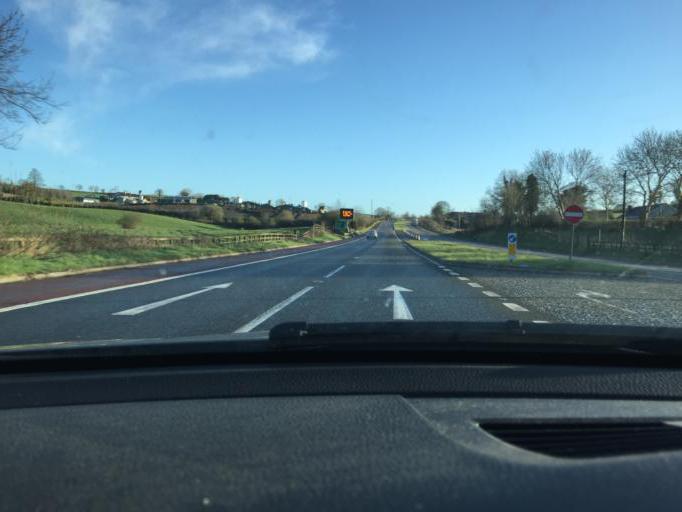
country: GB
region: Northern Ireland
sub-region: Banbridge District
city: Banbridge
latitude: 54.3222
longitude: -6.2978
